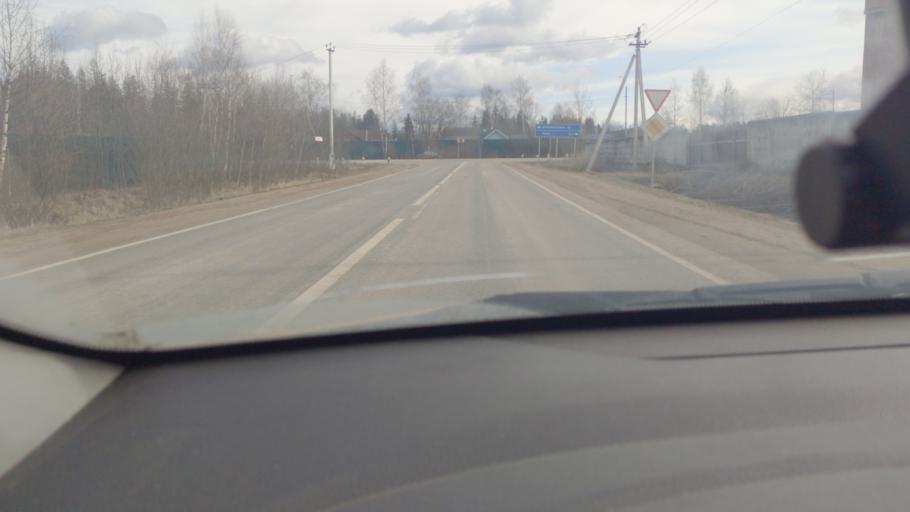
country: RU
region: Moskovskaya
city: Ruza
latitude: 55.7625
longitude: 36.1420
